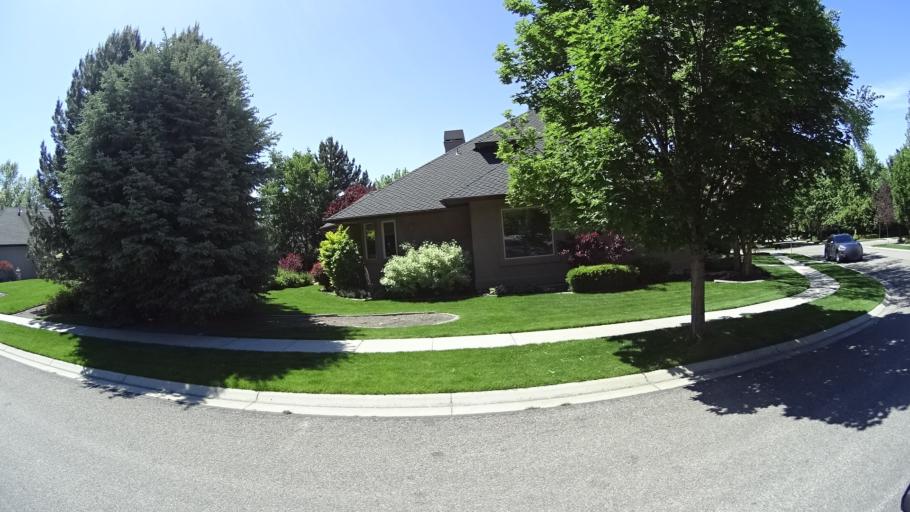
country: US
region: Idaho
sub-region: Ada County
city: Boise
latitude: 43.5727
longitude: -116.1158
